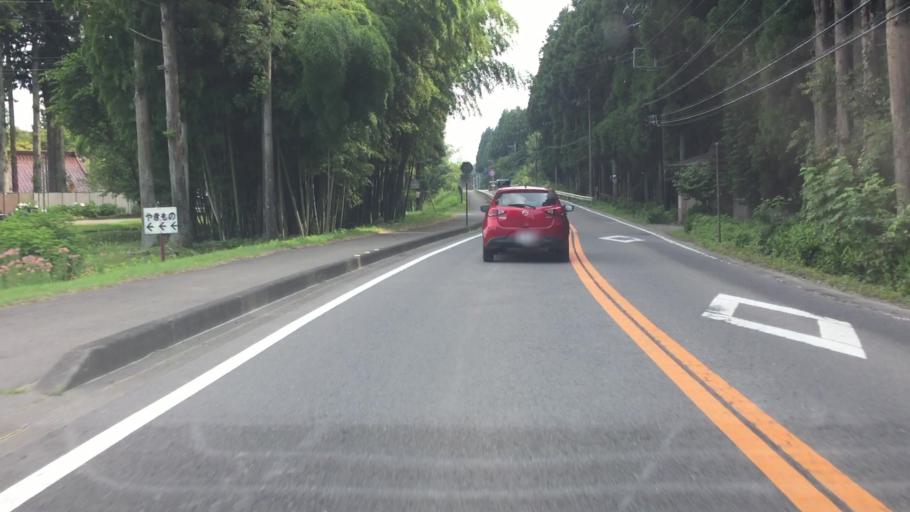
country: JP
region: Tochigi
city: Kuroiso
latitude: 37.0003
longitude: 139.9446
